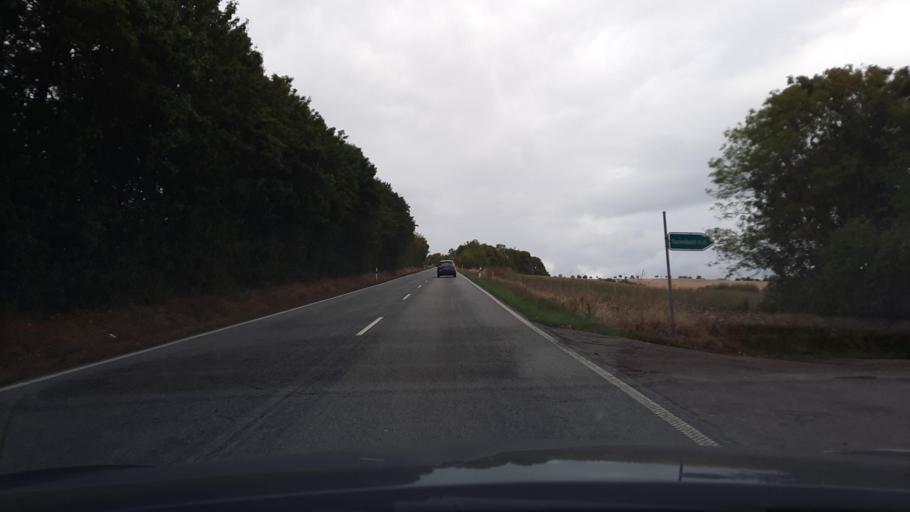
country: DE
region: Rheinland-Pfalz
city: Hockweiler
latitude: 49.6953
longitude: 6.7010
